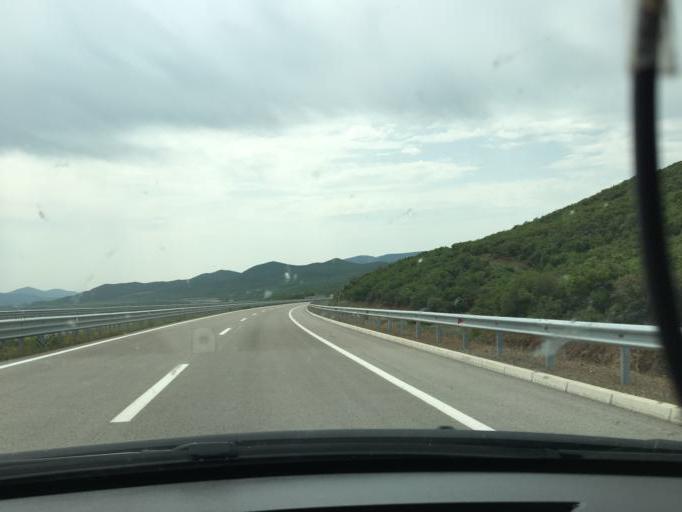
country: MK
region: Gevgelija
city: Miravci
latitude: 41.3068
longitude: 22.4266
